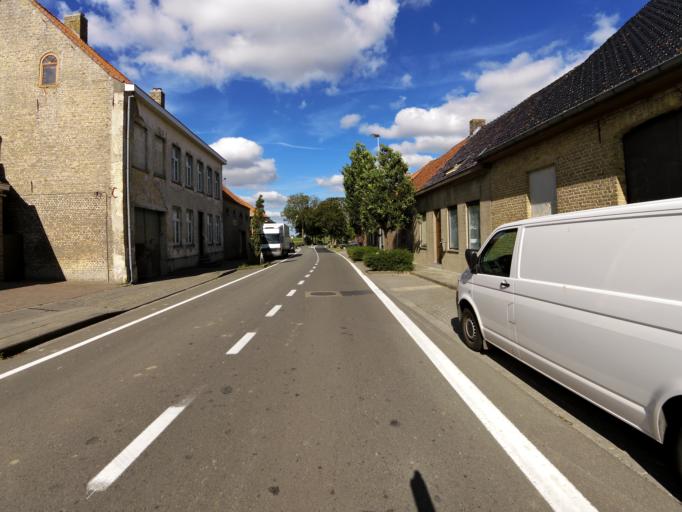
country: BE
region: Flanders
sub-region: Provincie West-Vlaanderen
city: Alveringem
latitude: 50.9703
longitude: 2.6782
